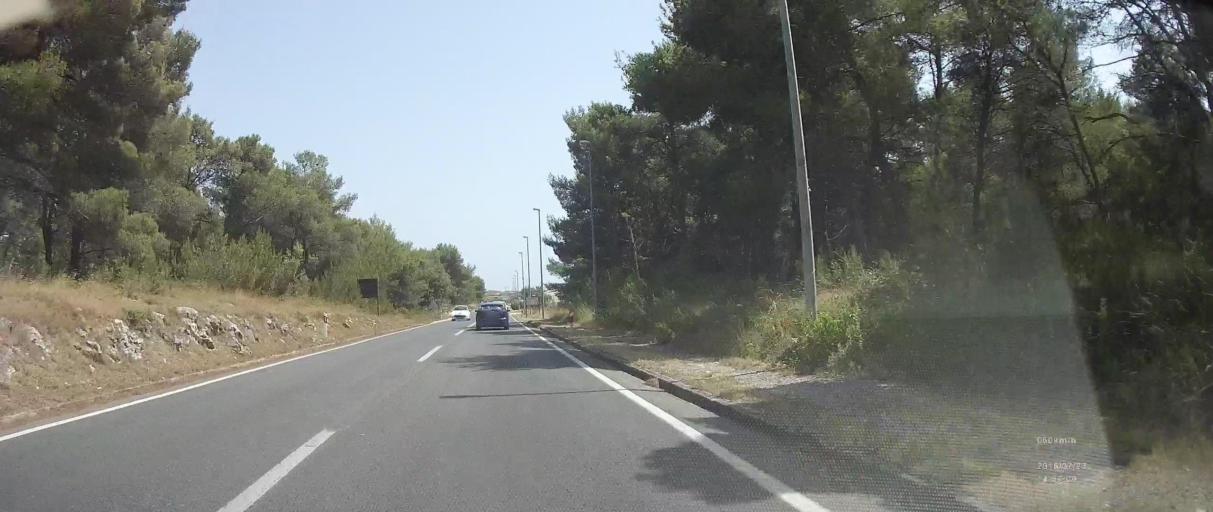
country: HR
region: Zadarska
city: Biograd na Moru
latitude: 43.9470
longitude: 15.4522
